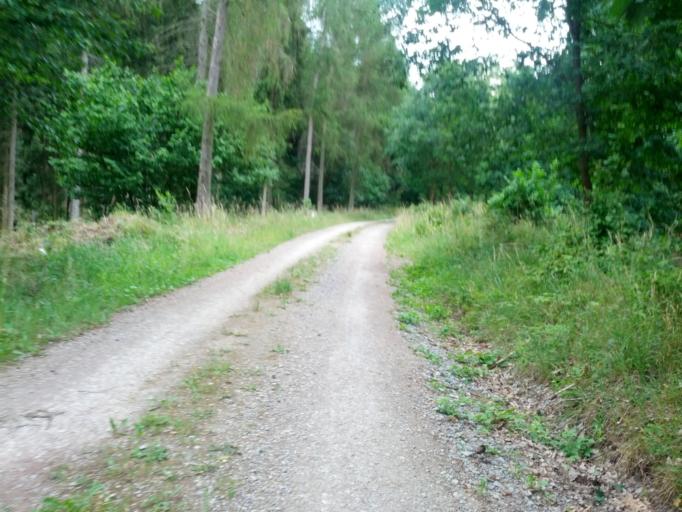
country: DE
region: Thuringia
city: Krauthausen
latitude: 50.9786
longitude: 10.2727
